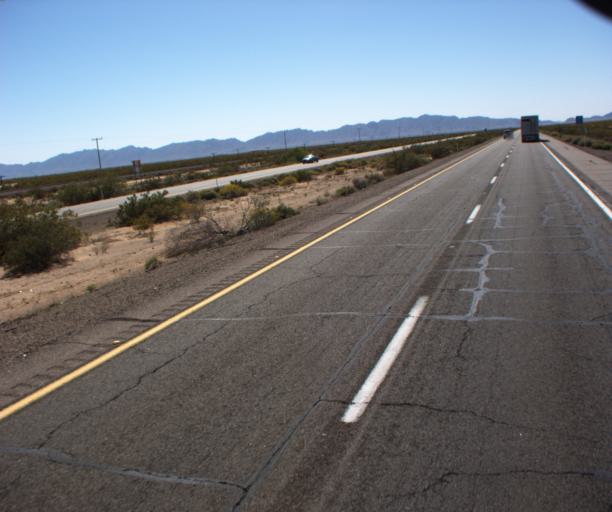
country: US
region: Arizona
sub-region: Yuma County
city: Wellton
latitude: 32.7835
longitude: -113.5761
